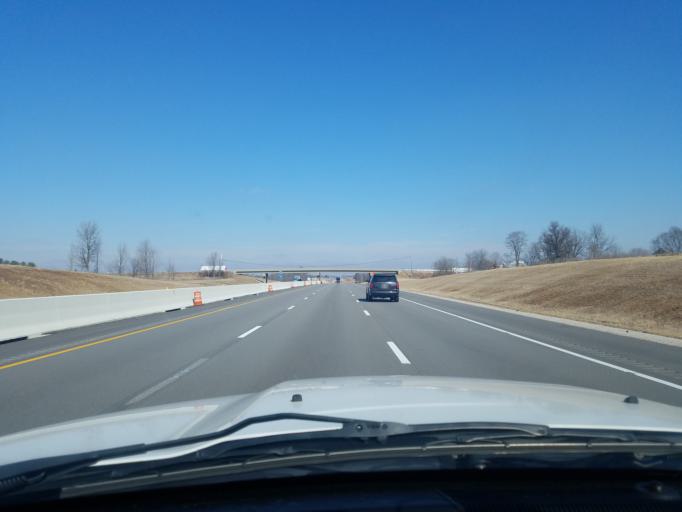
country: US
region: Kentucky
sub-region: Larue County
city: Hodgenville
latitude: 37.5364
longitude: -85.8815
